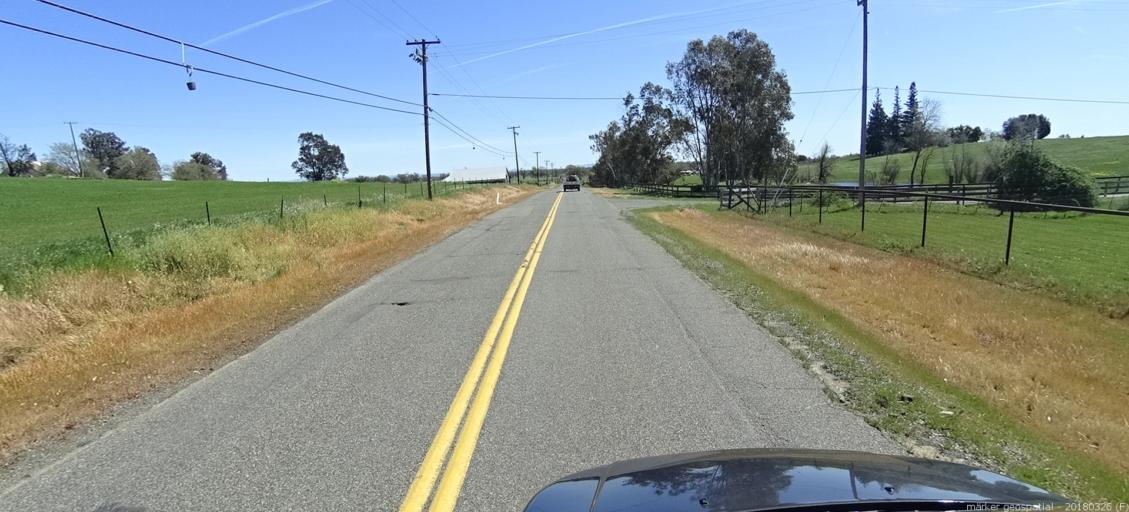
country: US
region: California
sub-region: Sacramento County
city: Wilton
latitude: 38.4653
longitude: -121.2436
